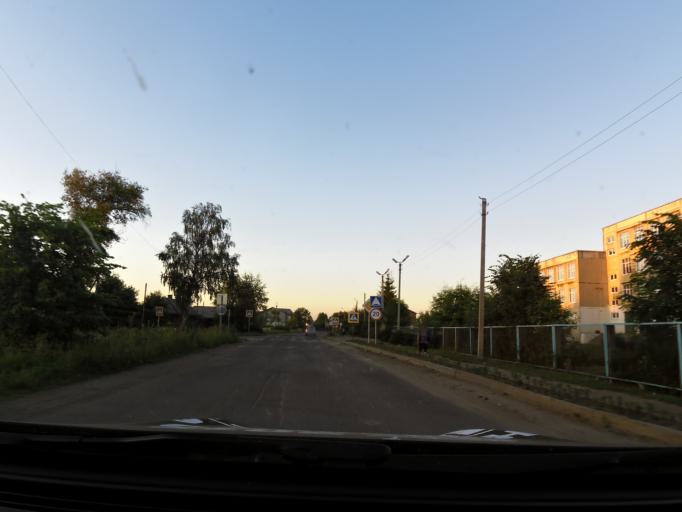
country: RU
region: Jaroslavl
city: Lyubim
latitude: 58.3572
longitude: 40.6950
